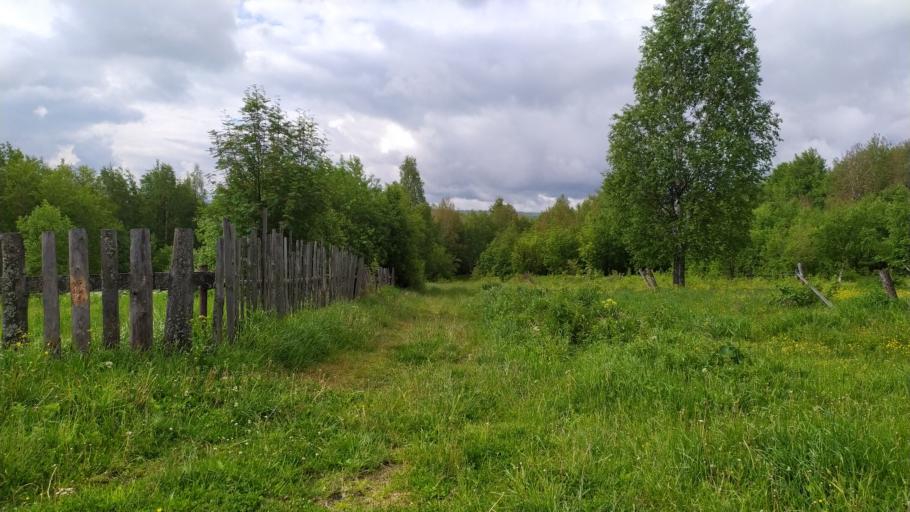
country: RU
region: Perm
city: Gremyachinsk
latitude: 58.5264
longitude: 57.8607
